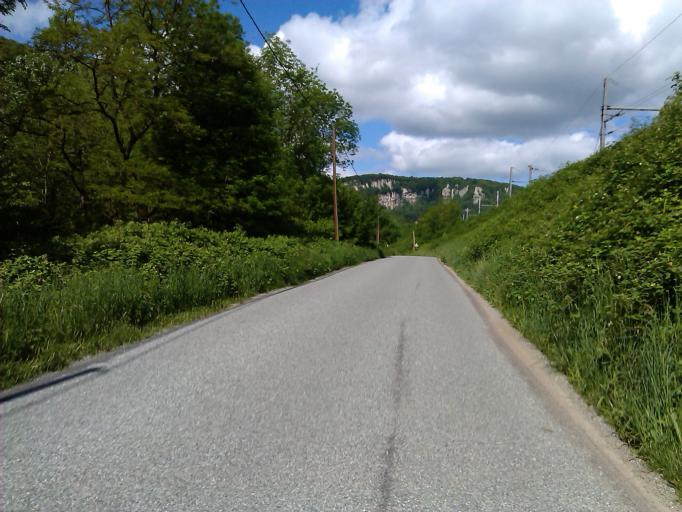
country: FR
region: Franche-Comte
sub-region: Departement du Doubs
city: Roulans
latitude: 47.2982
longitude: 6.2262
